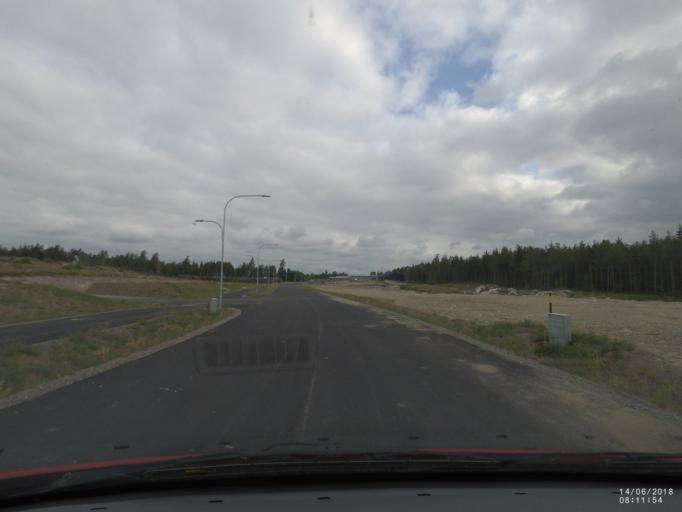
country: SE
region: Soedermanland
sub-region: Oxelosunds Kommun
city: Bara
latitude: 58.7131
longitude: 17.0351
